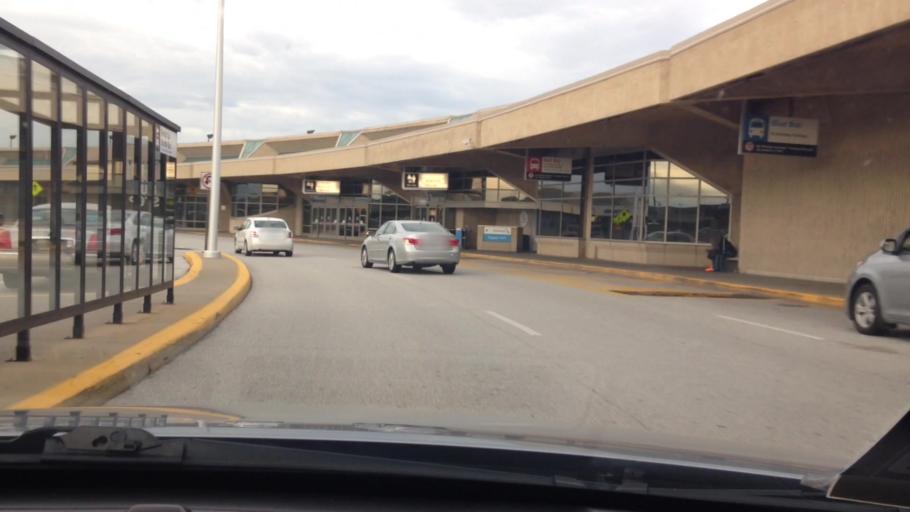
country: US
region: Missouri
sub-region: Platte County
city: Weatherby Lake
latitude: 39.2940
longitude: -94.7121
